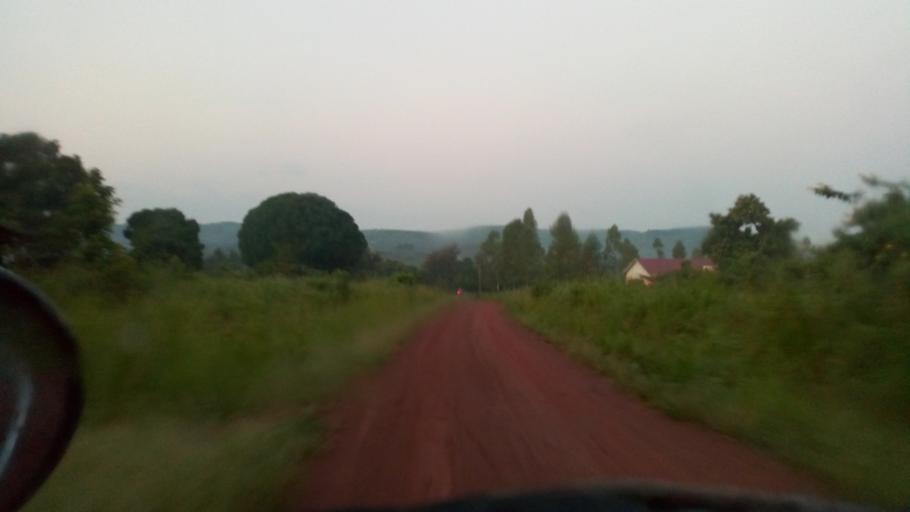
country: UG
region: Western Region
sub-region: Masindi District
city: Masindi
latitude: 1.6736
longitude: 31.7415
